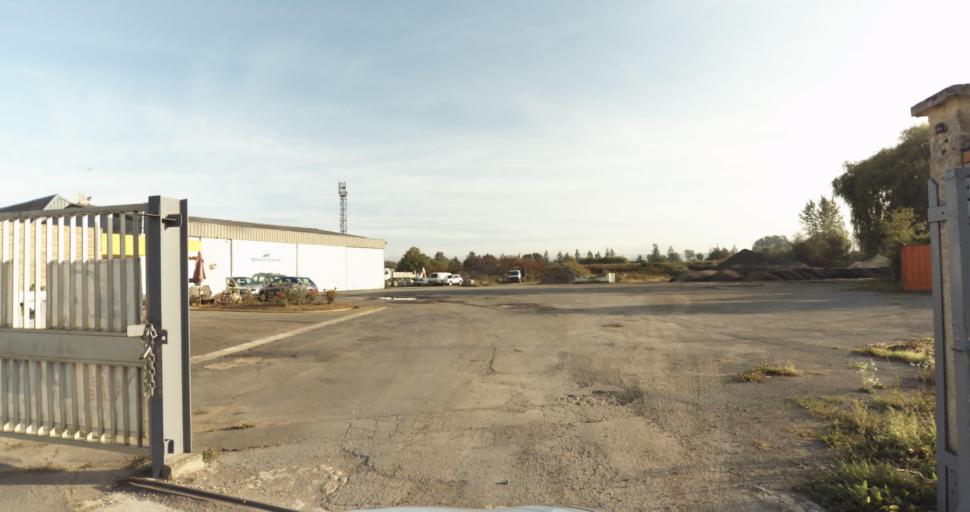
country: FR
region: Champagne-Ardenne
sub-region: Departement des Ardennes
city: Villers-Semeuse
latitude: 49.7412
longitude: 4.7566
